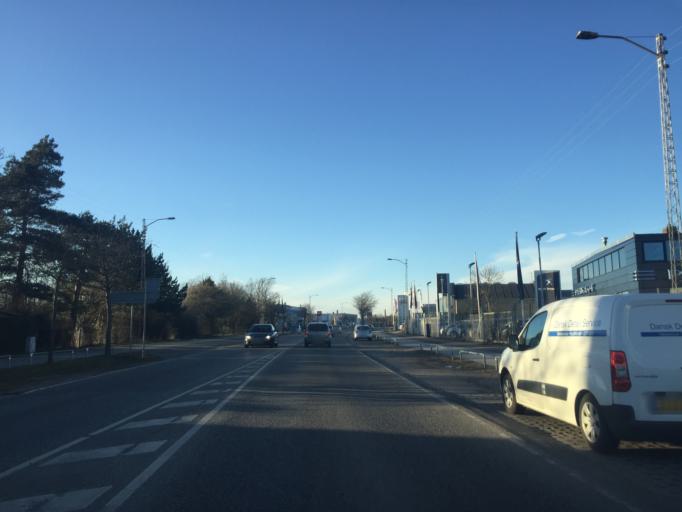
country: DK
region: Capital Region
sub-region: Tarnby Kommune
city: Tarnby
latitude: 55.6193
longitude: 12.6055
